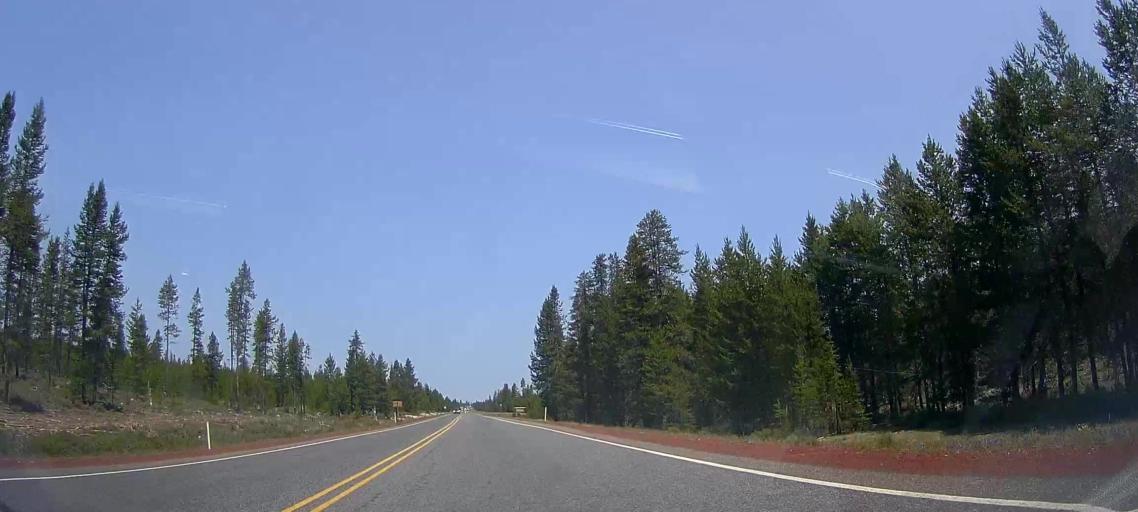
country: US
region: Oregon
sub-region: Deschutes County
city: La Pine
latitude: 43.3843
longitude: -121.7300
